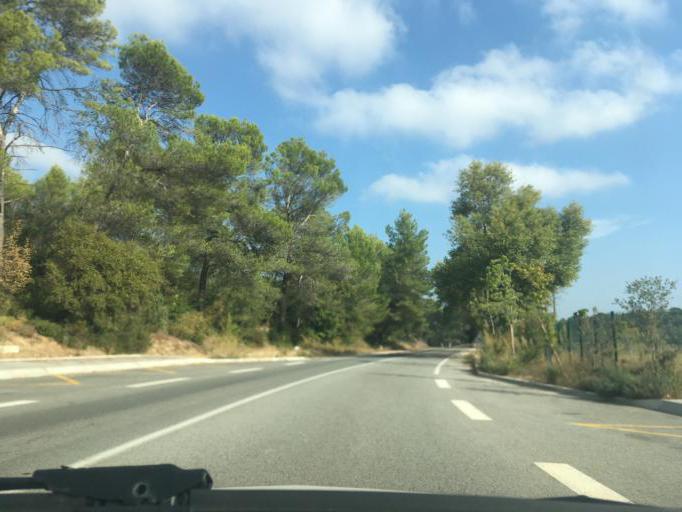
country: FR
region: Provence-Alpes-Cote d'Azur
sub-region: Departement du Var
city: Flayosc
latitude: 43.5026
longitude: 6.4198
